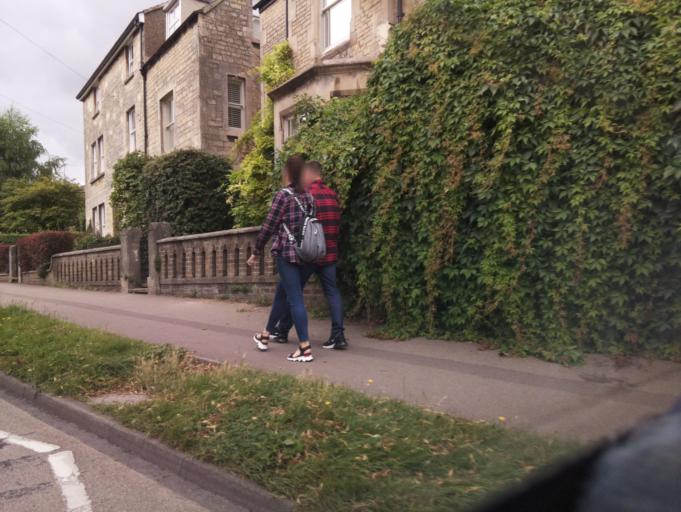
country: GB
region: England
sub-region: Lincolnshire
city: Stamford
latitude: 52.6553
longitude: -0.4700
